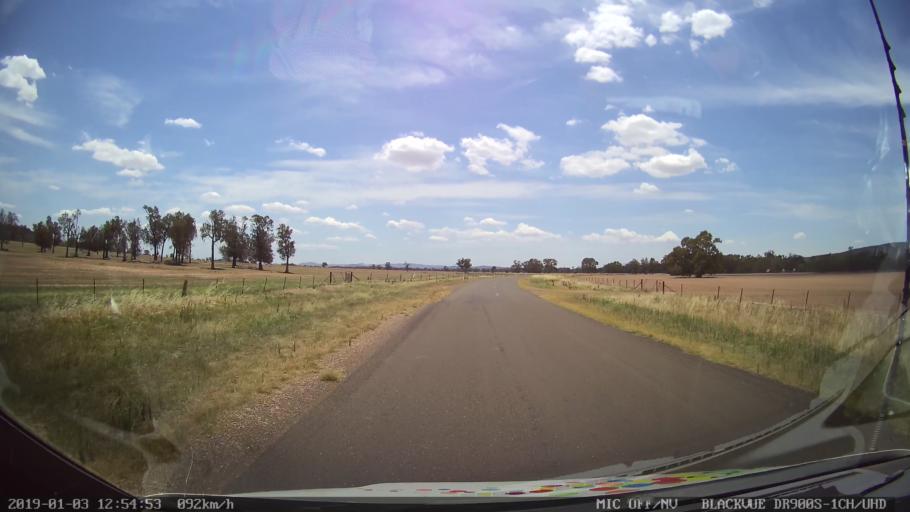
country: AU
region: New South Wales
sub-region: Weddin
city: Grenfell
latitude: -33.6484
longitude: 148.3225
